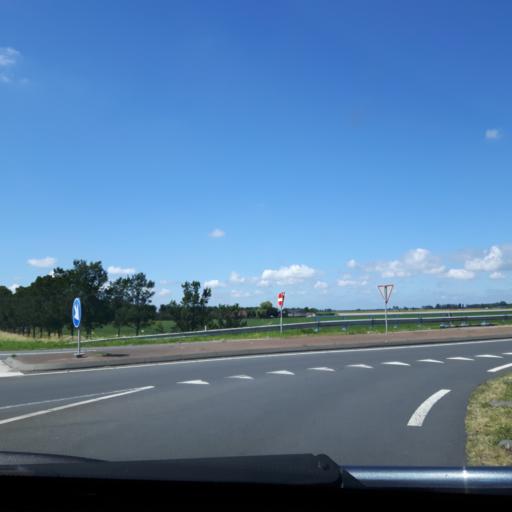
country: NL
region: Zeeland
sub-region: Gemeente Goes
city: Goes
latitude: 51.5682
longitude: 3.8496
